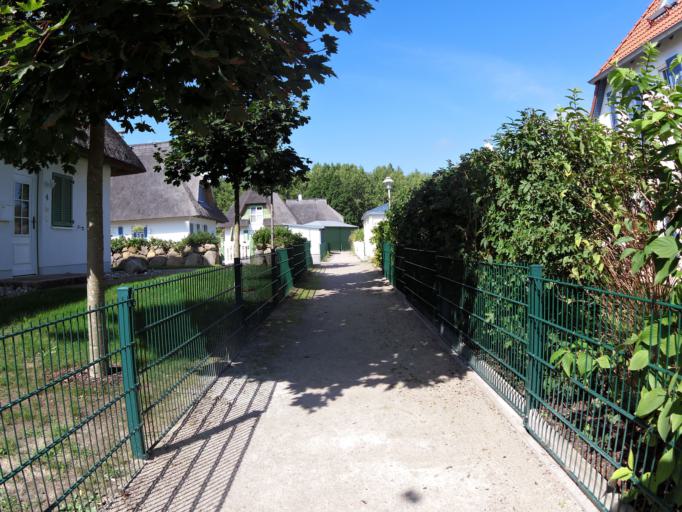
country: DE
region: Mecklenburg-Vorpommern
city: Karlshagen
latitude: 54.1278
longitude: 13.8330
